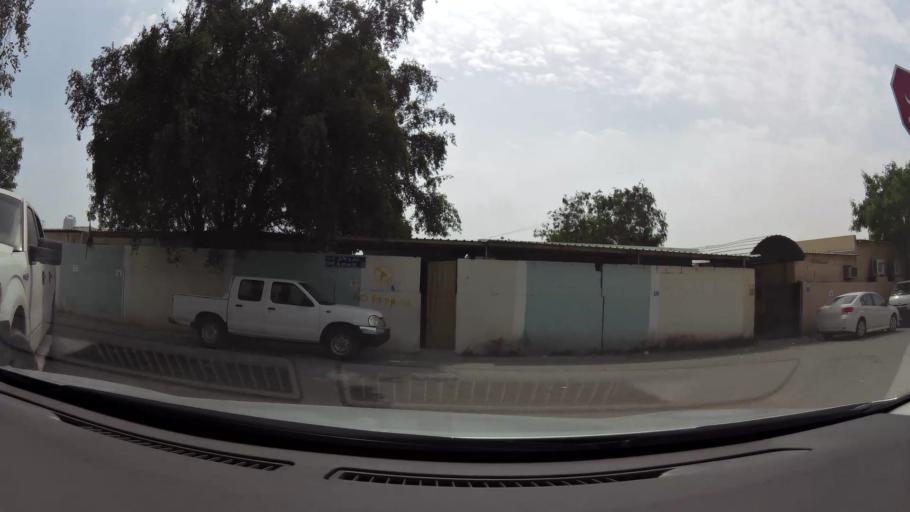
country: QA
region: Baladiyat ad Dawhah
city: Doha
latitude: 25.2643
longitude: 51.4943
